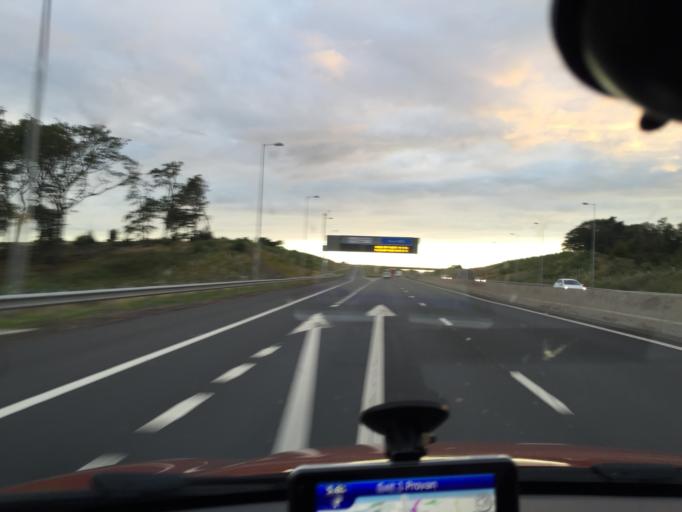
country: GB
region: Scotland
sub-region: North Lanarkshire
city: Chryston
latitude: 55.9049
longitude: -4.1308
